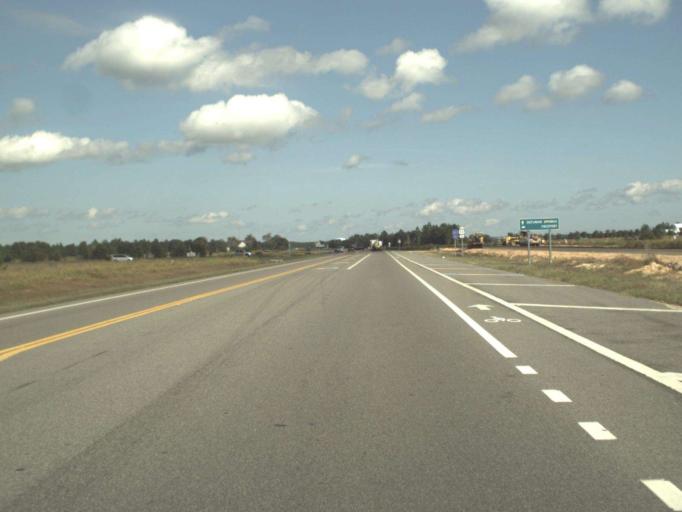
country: US
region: Florida
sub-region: Walton County
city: Freeport
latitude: 30.5500
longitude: -86.1066
